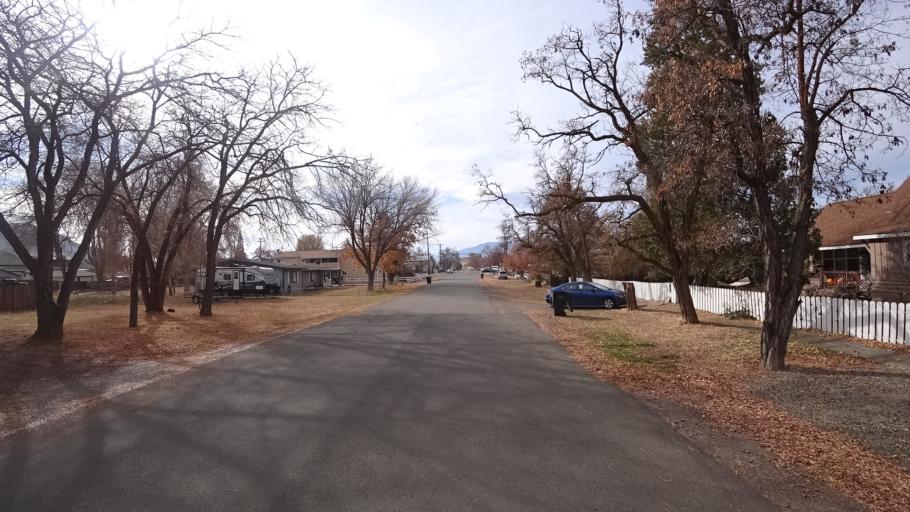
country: US
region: California
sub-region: Siskiyou County
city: Montague
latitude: 41.7297
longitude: -122.5284
